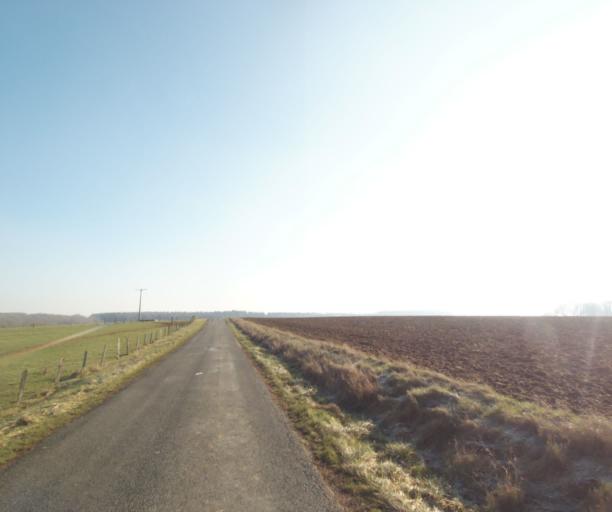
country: FR
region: Champagne-Ardenne
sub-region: Departement de la Haute-Marne
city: Bienville
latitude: 48.5029
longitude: 5.0404
